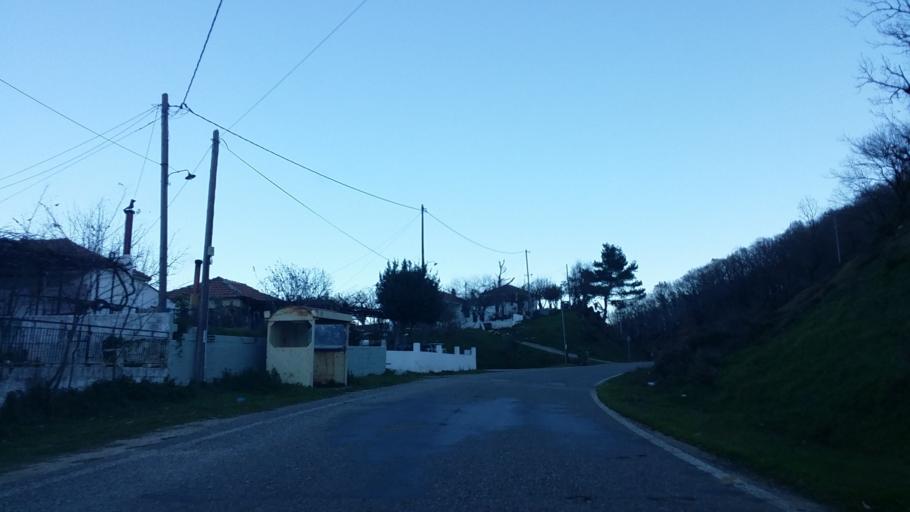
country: GR
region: West Greece
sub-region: Nomos Aitolias kai Akarnanias
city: Sardinia
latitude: 38.8660
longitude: 21.2946
